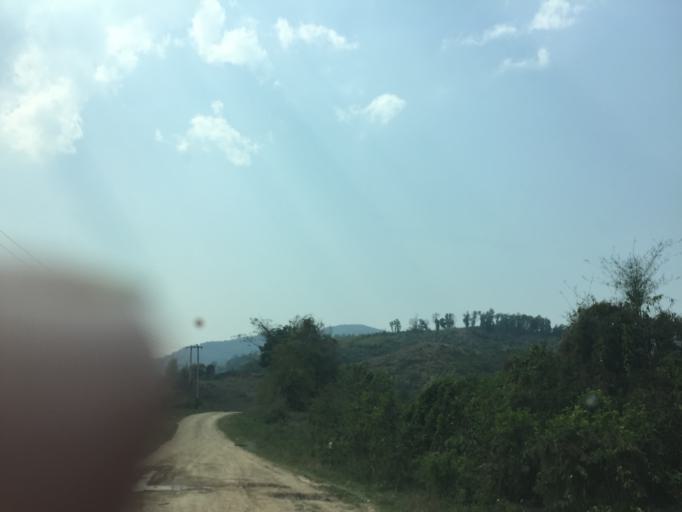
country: TH
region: Nan
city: Song Khwae
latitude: 19.7387
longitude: 100.7169
